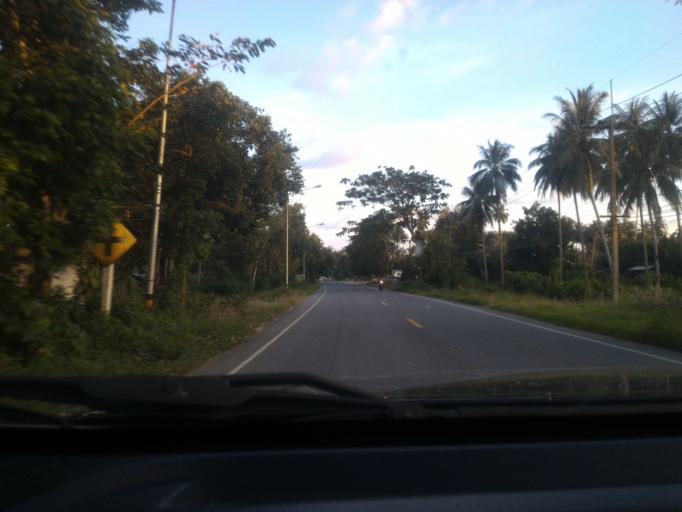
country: TH
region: Surat Thani
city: Don Sak
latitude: 9.0475
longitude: 99.9025
